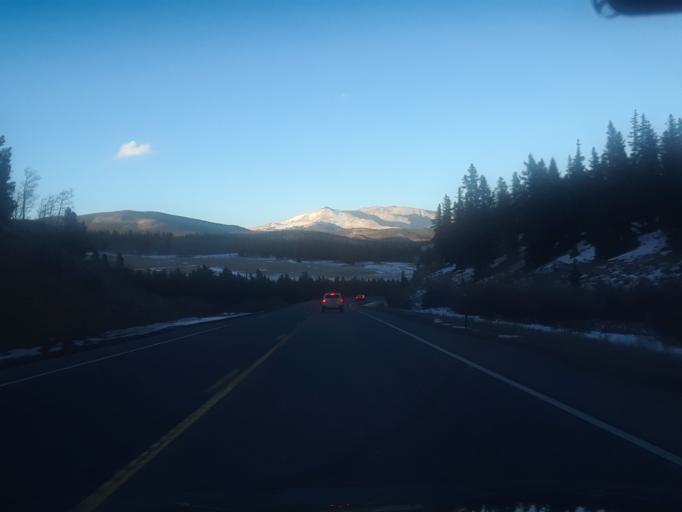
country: US
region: Colorado
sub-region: Summit County
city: Breckenridge
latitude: 39.4295
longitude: -105.7632
